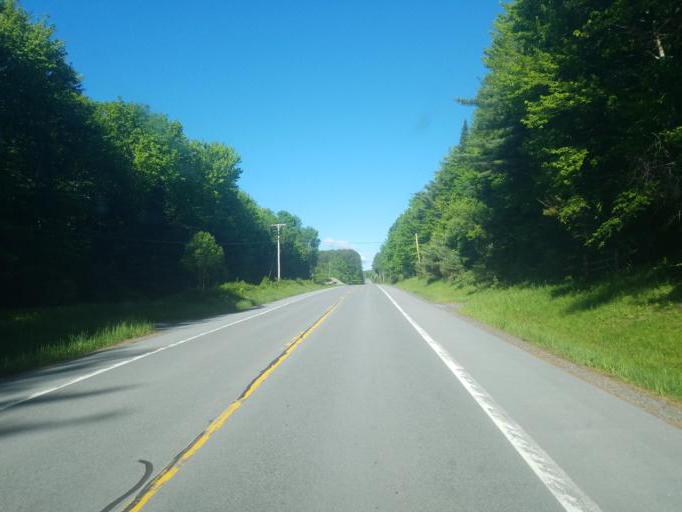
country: US
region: New York
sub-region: Oneida County
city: Utica
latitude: 43.3530
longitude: -75.0499
